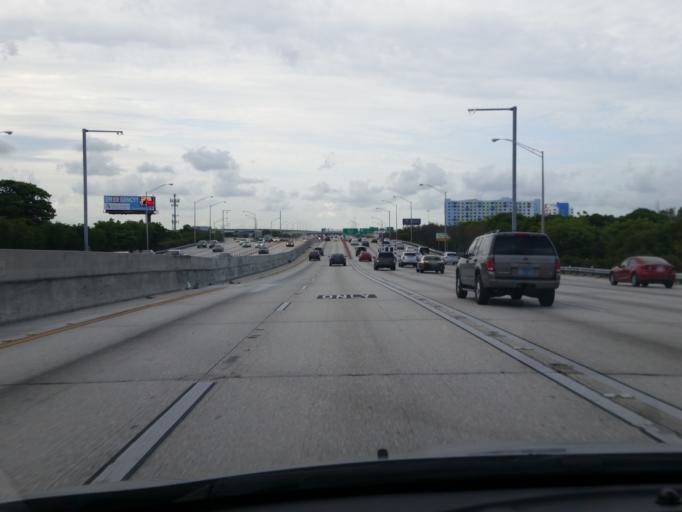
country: US
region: Florida
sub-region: Miami-Dade County
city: Allapattah
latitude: 25.8041
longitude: -80.2057
